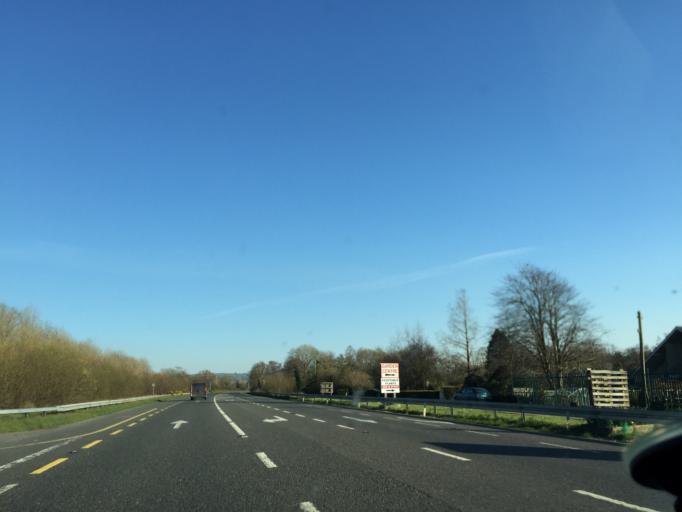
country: IE
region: Munster
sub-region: Ciarrai
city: Castleisland
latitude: 52.1933
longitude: -9.5664
